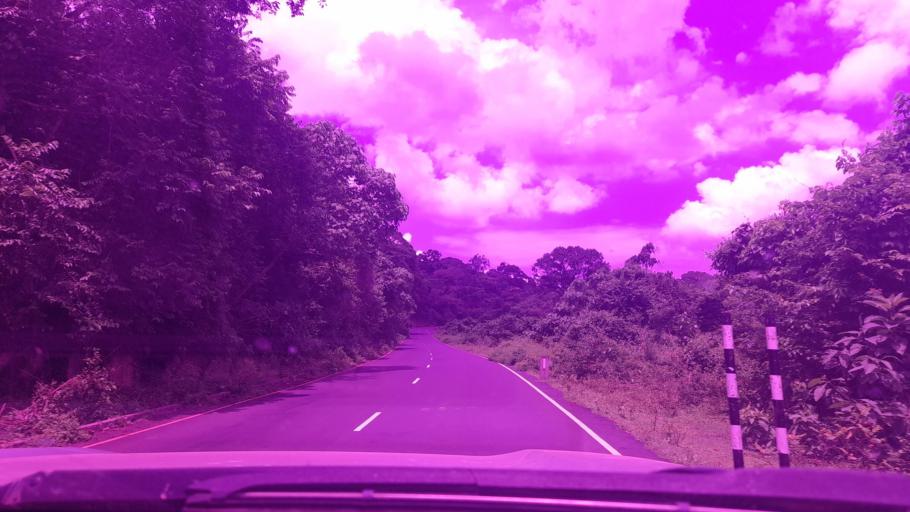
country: ET
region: Oromiya
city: Metu
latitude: 8.3316
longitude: 35.7670
